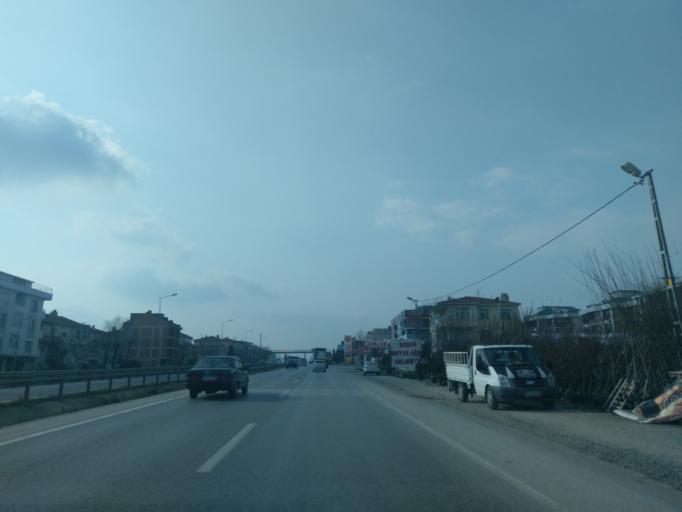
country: TR
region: Istanbul
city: Selimpasa
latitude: 41.0556
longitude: 28.3718
